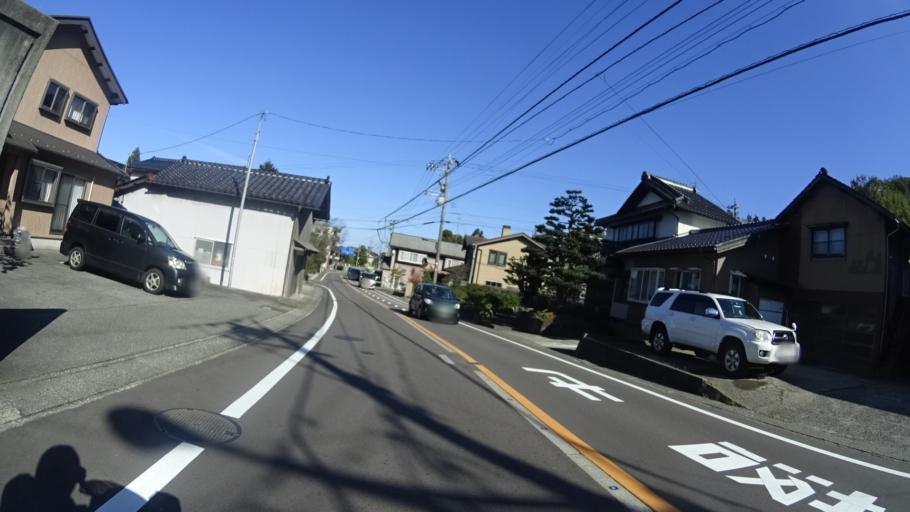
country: JP
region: Ishikawa
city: Nonoichi
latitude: 36.5004
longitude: 136.6225
